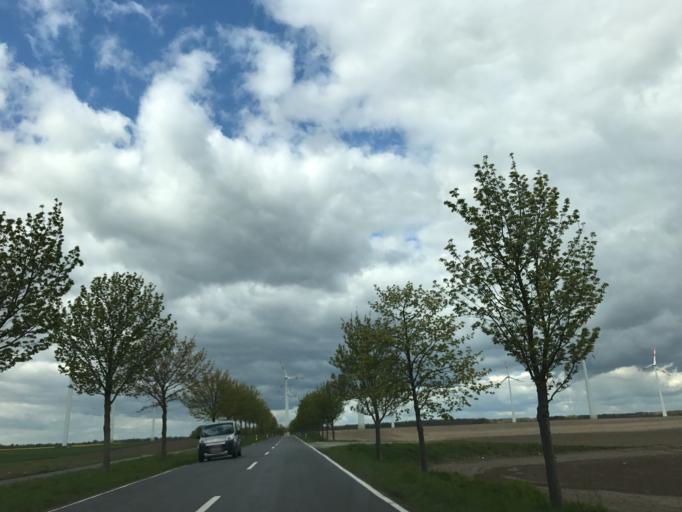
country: DE
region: Brandenburg
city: Nauen
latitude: 52.5917
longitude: 12.8094
